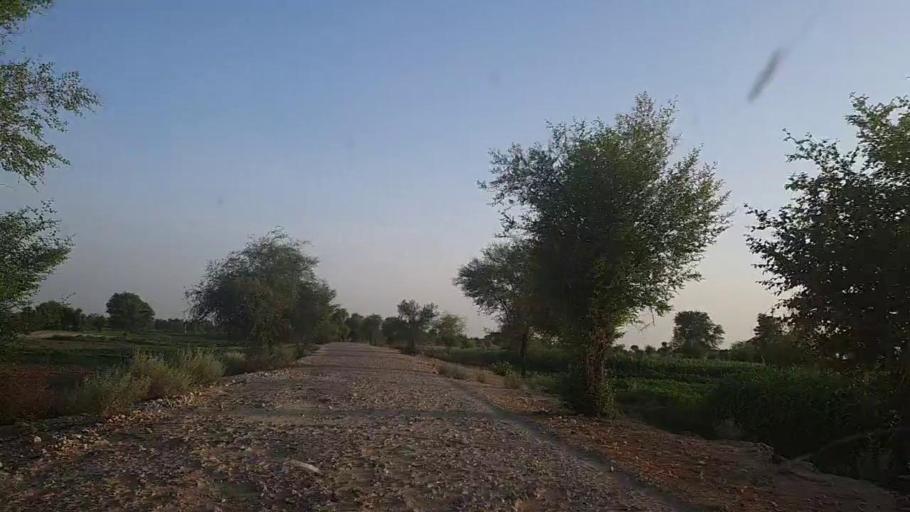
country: PK
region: Sindh
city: Khanpur
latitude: 27.6339
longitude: 69.4478
